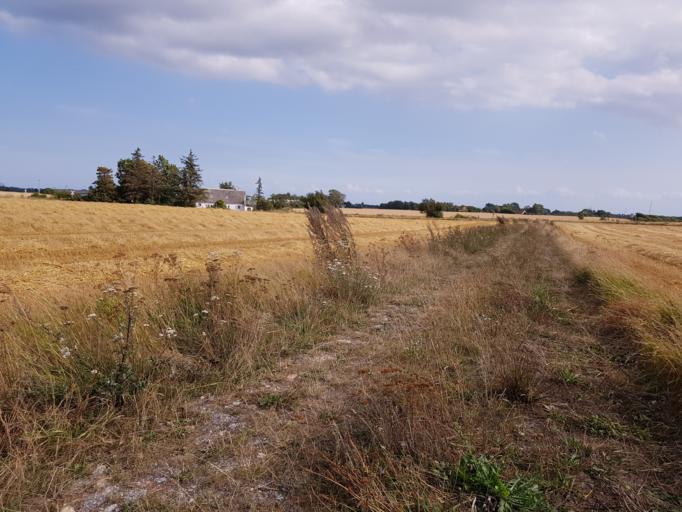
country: DK
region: Zealand
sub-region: Guldborgsund Kommune
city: Nykobing Falster
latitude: 54.5956
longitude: 11.9253
